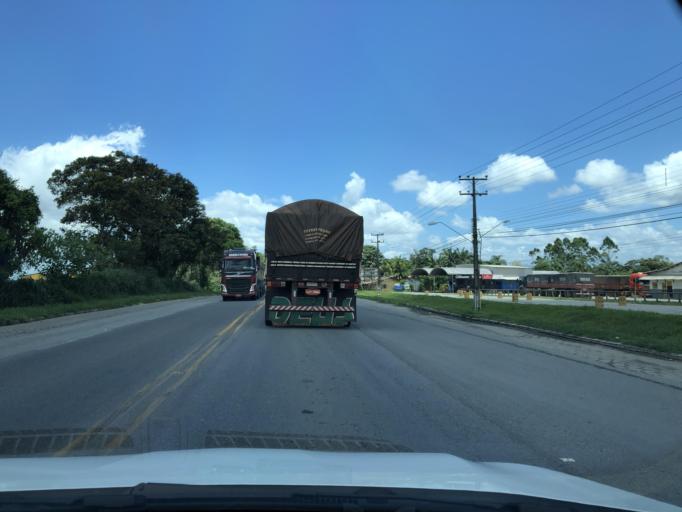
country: BR
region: Santa Catarina
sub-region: Sao Francisco Do Sul
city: Sao Francisco do Sul
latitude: -26.3712
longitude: -48.7071
